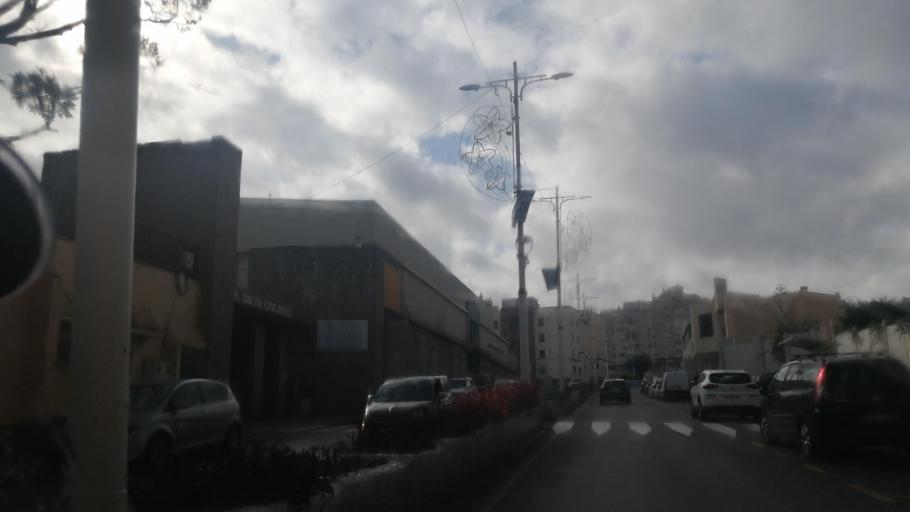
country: ES
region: Ceuta
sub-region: Ceuta
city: Ceuta
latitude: 35.8877
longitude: -5.3227
